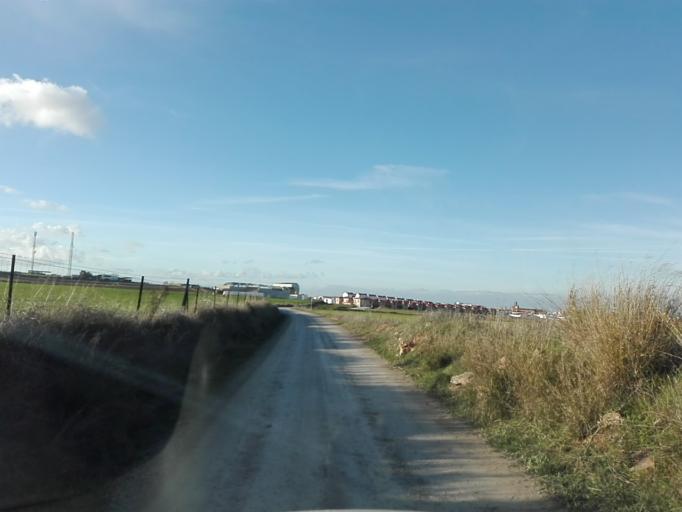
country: ES
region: Extremadura
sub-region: Provincia de Badajoz
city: Llerena
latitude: 38.2288
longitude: -6.0122
